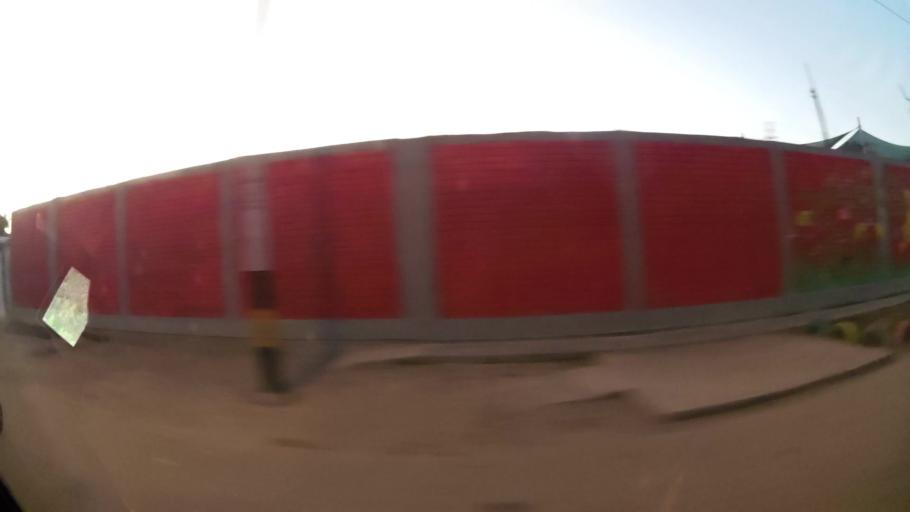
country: PE
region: Ica
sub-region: Provincia de Ica
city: Ica
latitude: -14.0784
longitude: -75.7335
